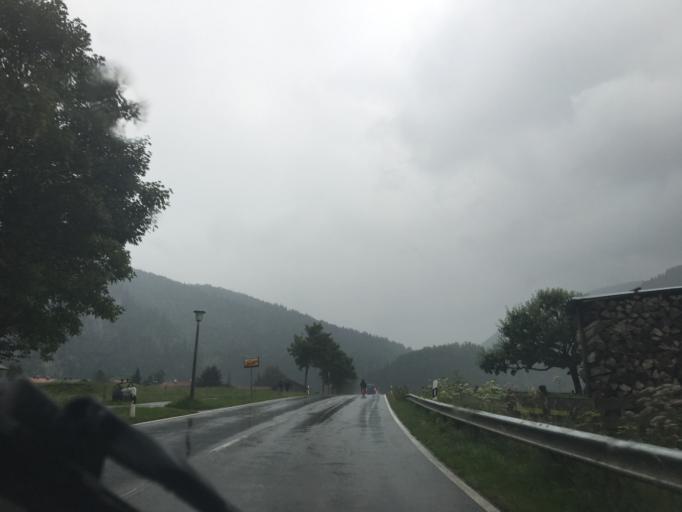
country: DE
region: Bavaria
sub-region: Upper Bavaria
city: Unterwossen
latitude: 47.7137
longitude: 12.4777
